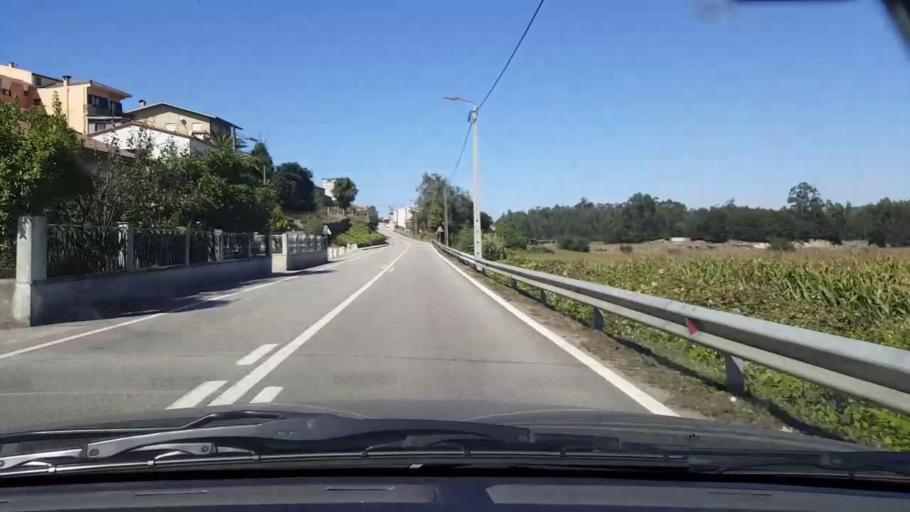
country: PT
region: Porto
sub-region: Maia
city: Gemunde
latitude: 41.3385
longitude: -8.6367
